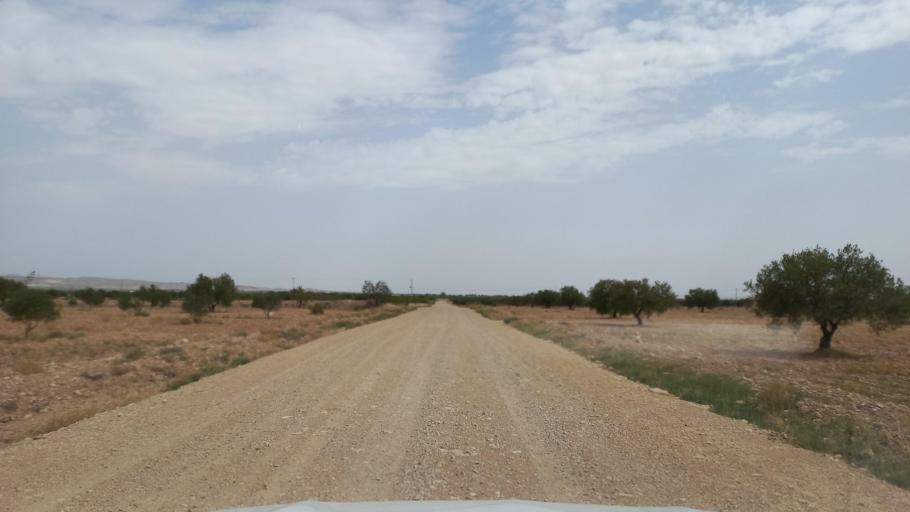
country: TN
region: Al Qasrayn
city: Kasserine
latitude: 35.2790
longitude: 9.0157
